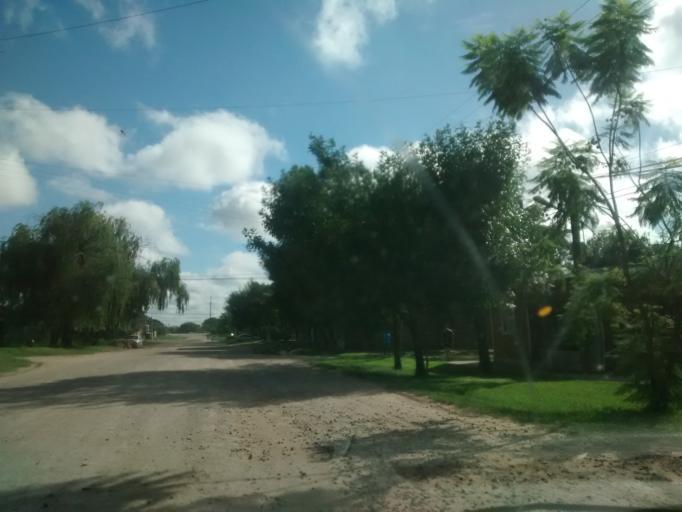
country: AR
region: Chaco
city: Resistencia
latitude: -27.4382
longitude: -58.9633
